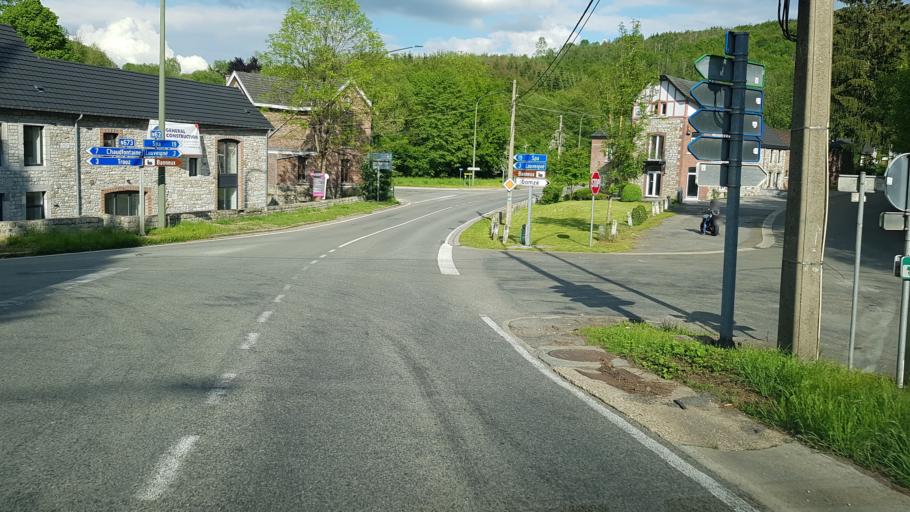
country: BE
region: Wallonia
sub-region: Province de Liege
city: Trooz
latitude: 50.5441
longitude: 5.6900
